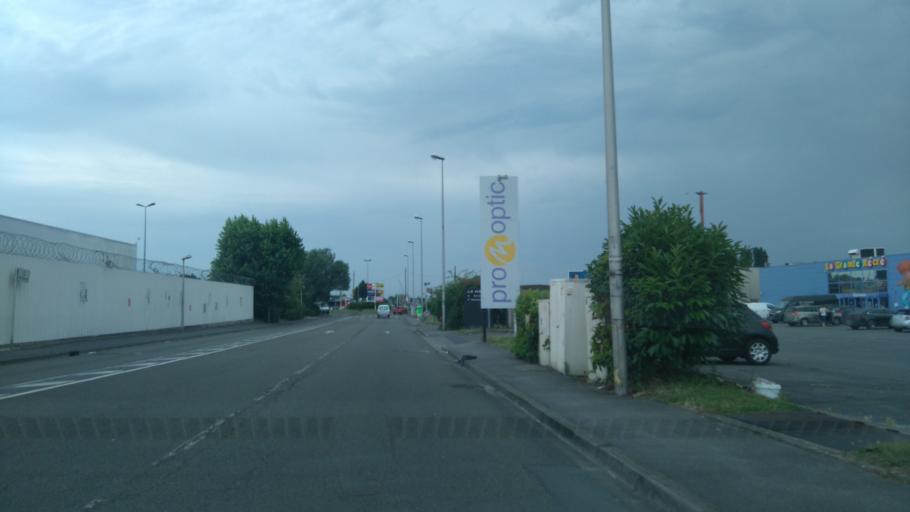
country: FR
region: Picardie
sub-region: Departement de l'Oise
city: Saint-Maximin
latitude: 49.2357
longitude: 2.4680
